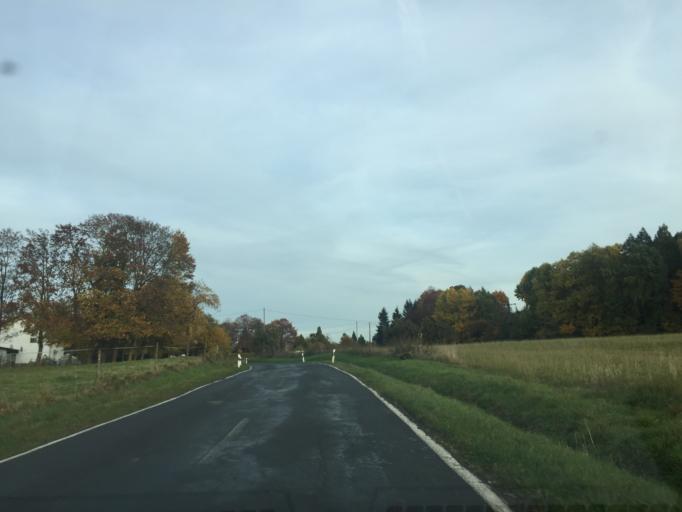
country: DE
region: Rheinland-Pfalz
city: Obererbach
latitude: 50.4597
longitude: 7.9693
